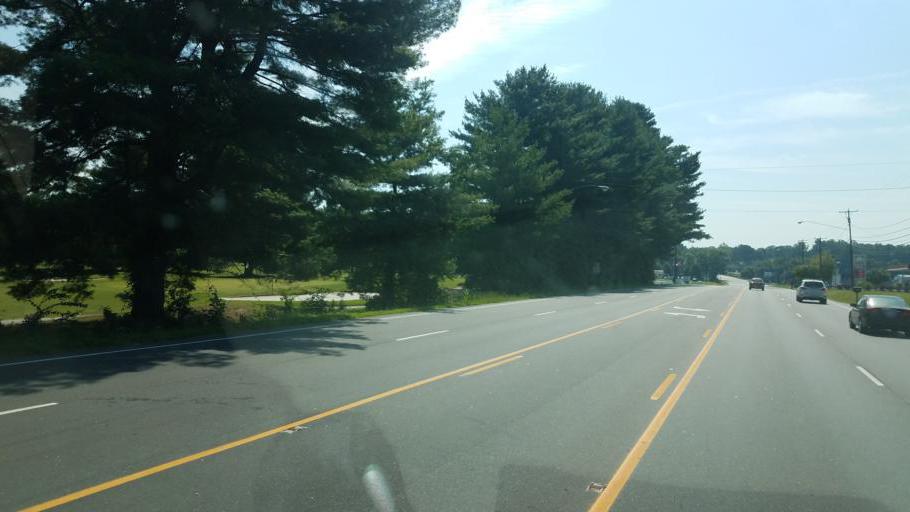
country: US
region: North Carolina
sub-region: Burke County
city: Morganton
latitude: 35.7519
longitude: -81.7121
